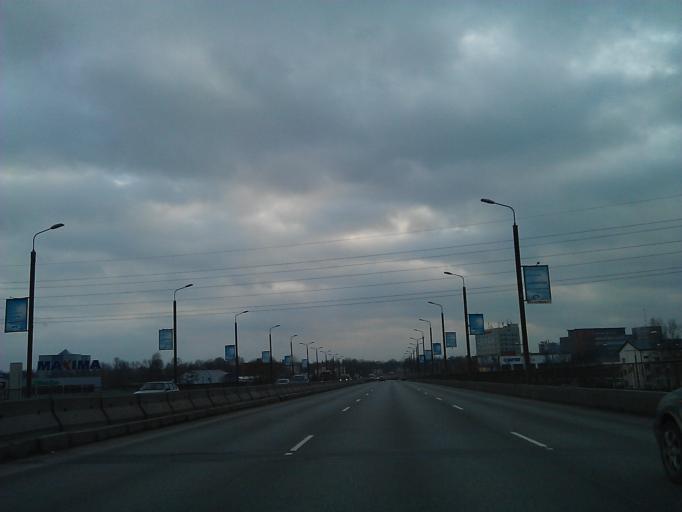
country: LV
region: Riga
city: Riga
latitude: 56.9250
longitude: 24.1073
